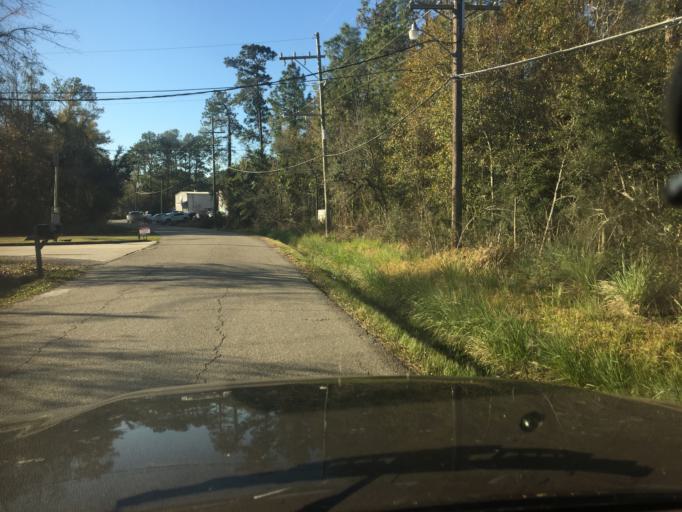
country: US
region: Louisiana
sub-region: Saint Tammany Parish
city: Slidell
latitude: 30.2469
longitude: -89.7660
